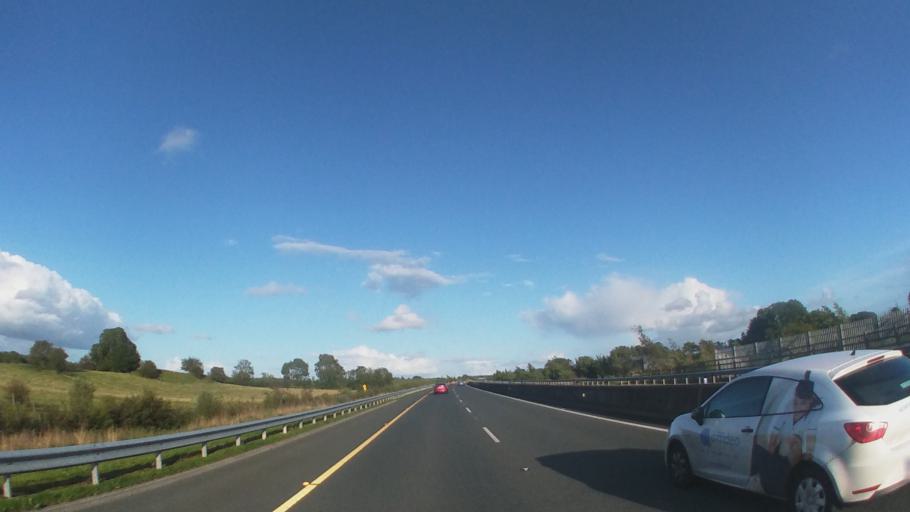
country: IE
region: Connaught
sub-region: County Galway
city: Loughrea
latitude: 53.2857
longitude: -8.4632
